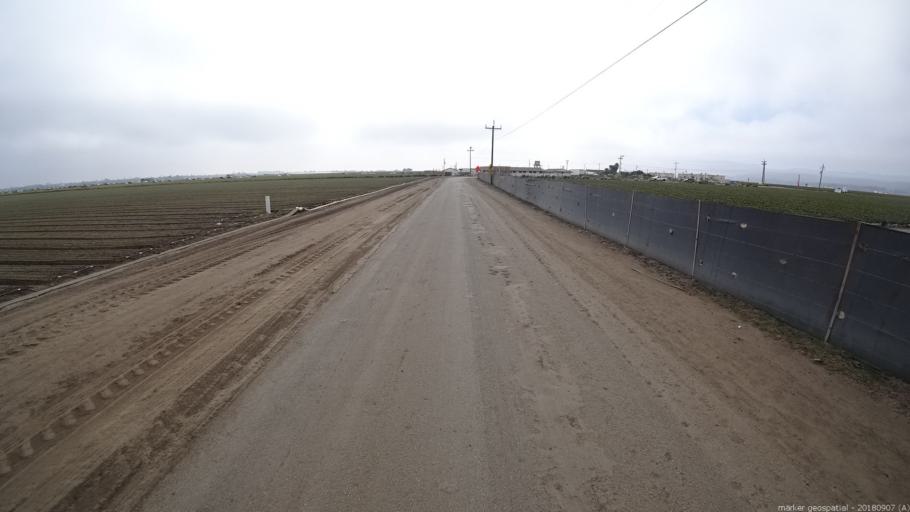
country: US
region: California
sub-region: Monterey County
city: Boronda
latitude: 36.6660
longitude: -121.7026
